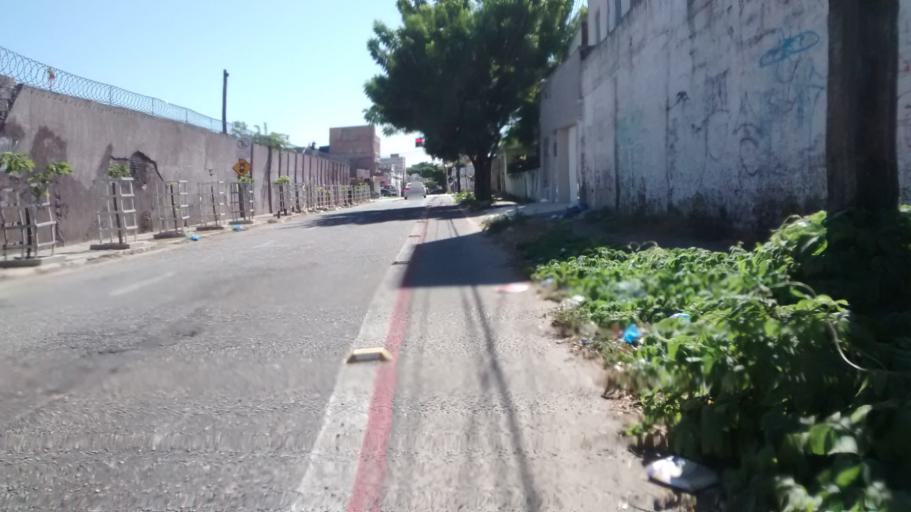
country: BR
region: Ceara
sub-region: Fortaleza
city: Fortaleza
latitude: -3.7395
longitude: -38.5192
